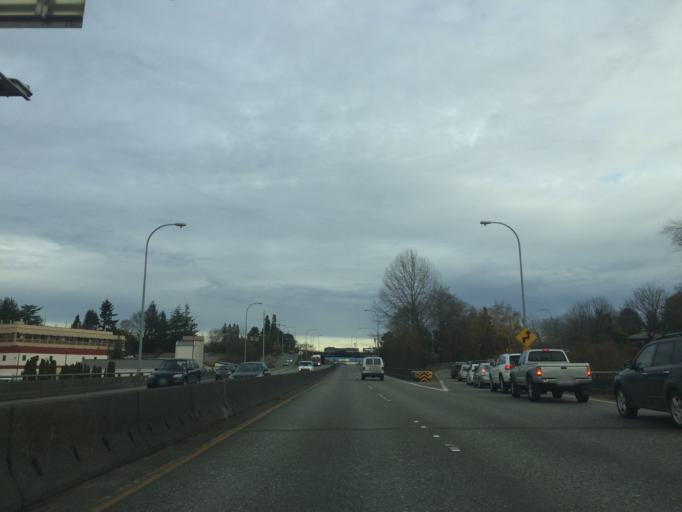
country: US
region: Washington
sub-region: King County
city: Seattle
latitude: 47.6434
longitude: -122.3086
